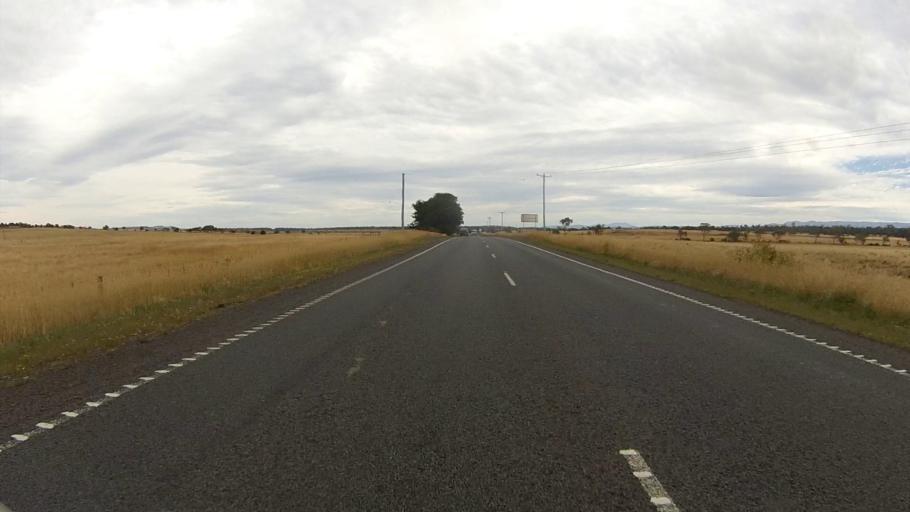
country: AU
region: Tasmania
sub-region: Northern Midlands
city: Evandale
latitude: -41.8662
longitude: 147.4581
